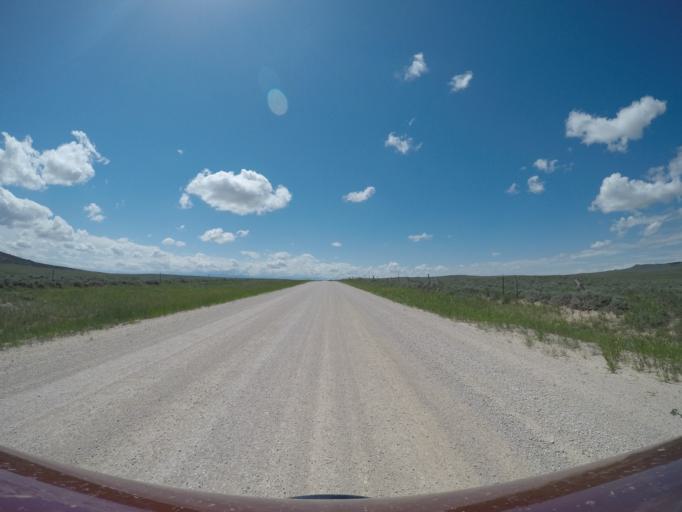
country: US
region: Wyoming
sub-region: Park County
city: Powell
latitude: 45.2050
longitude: -108.7343
